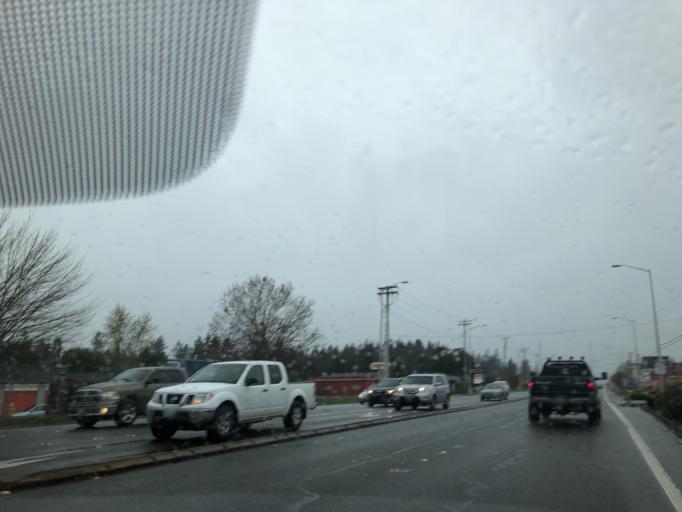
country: US
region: Washington
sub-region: Thurston County
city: Tanglewilde-Thompson Place
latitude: 47.0559
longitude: -122.7692
